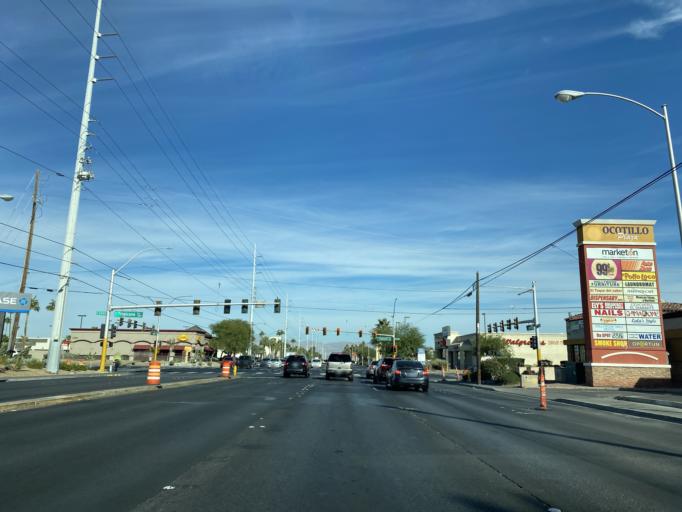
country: US
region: Nevada
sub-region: Clark County
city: Paradise
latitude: 36.0994
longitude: -115.1189
